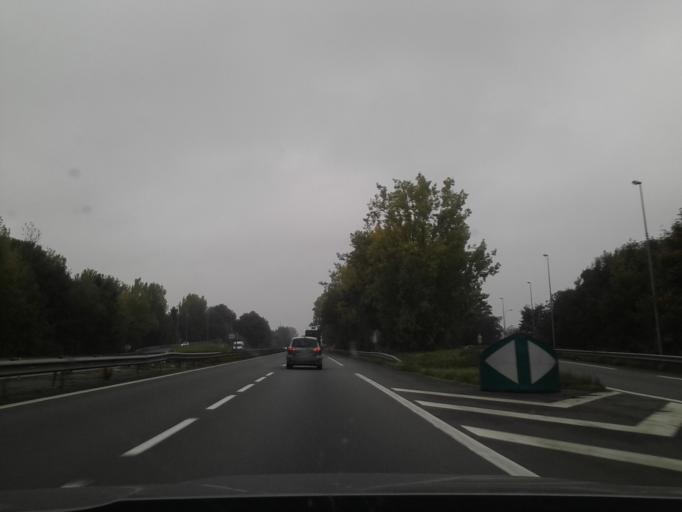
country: FR
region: Nord-Pas-de-Calais
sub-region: Departement du Nord
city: Lieu-Saint-Amand
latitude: 50.2700
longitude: 3.3339
